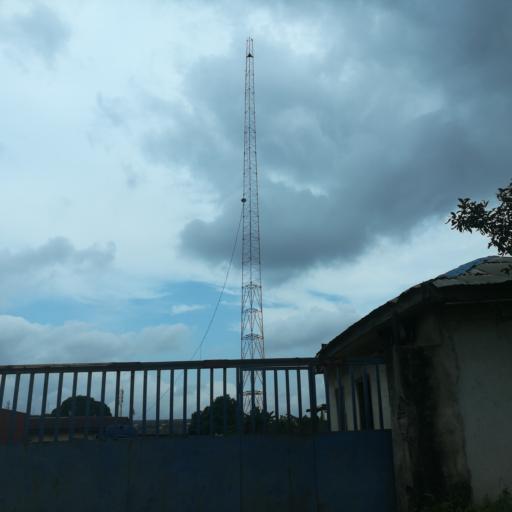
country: NG
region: Rivers
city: Port Harcourt
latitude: 4.8177
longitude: 7.0426
